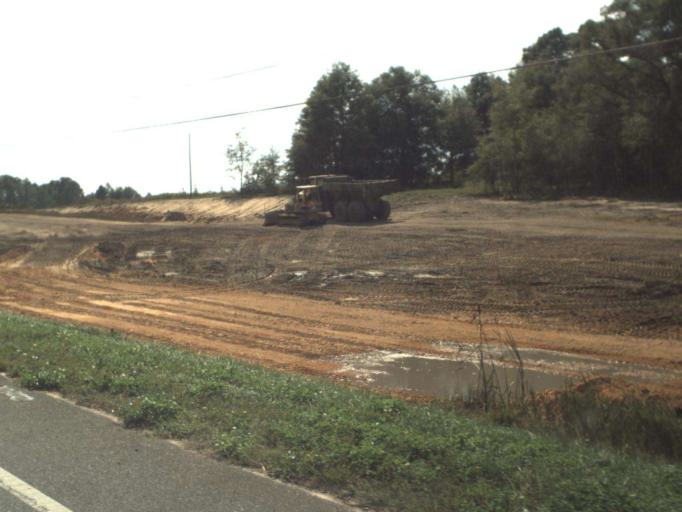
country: US
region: Florida
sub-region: Holmes County
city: Bonifay
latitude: 30.6854
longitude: -85.6865
